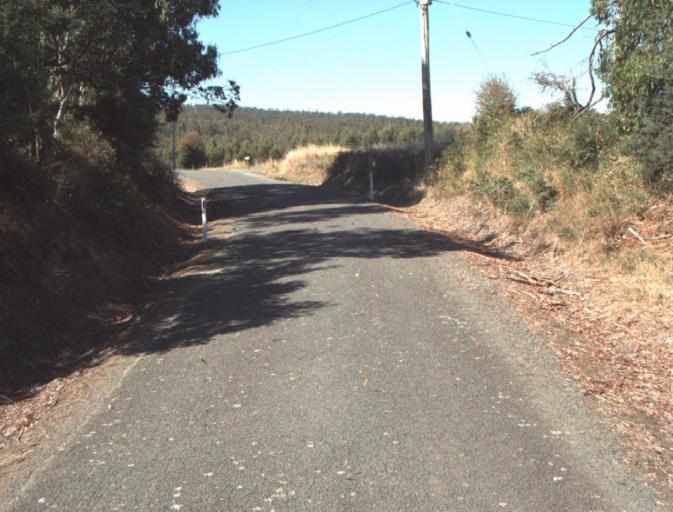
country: AU
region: Tasmania
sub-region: Launceston
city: Newstead
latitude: -41.3187
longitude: 147.3197
